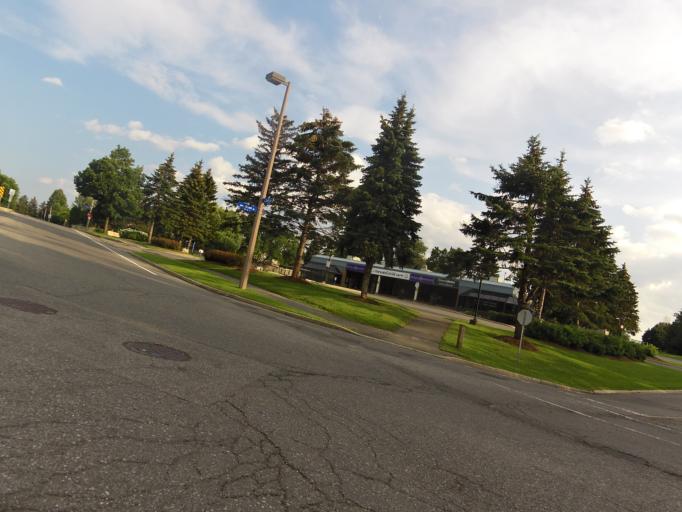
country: CA
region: Ontario
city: Bells Corners
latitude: 45.3055
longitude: -75.9058
